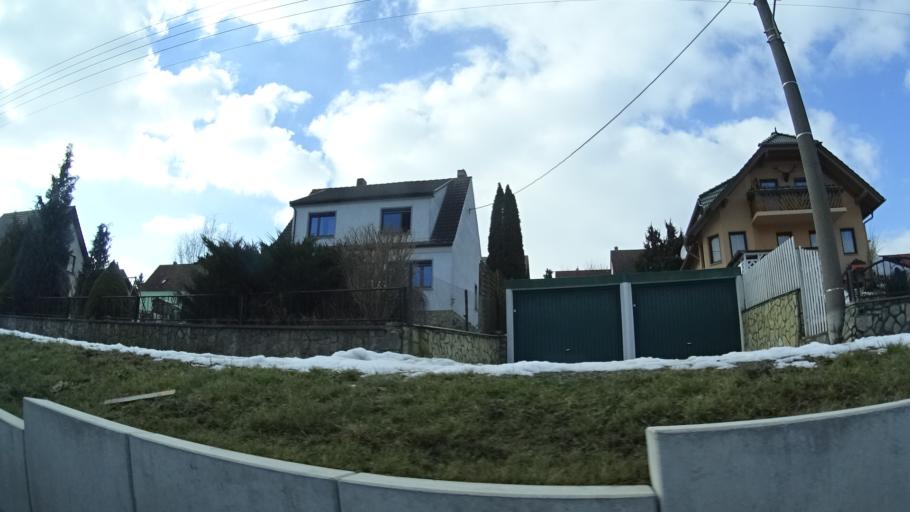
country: DE
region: Thuringia
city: Rippershausen
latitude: 50.5818
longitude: 10.3364
